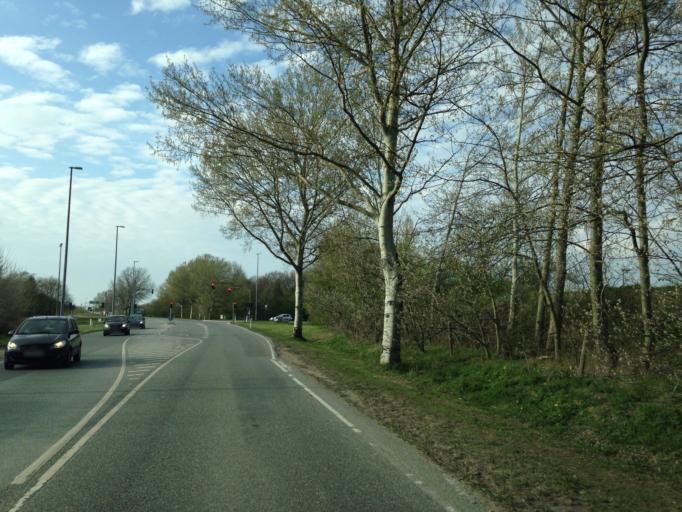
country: DK
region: Zealand
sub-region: Greve Kommune
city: Greve
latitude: 55.5775
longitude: 12.2637
